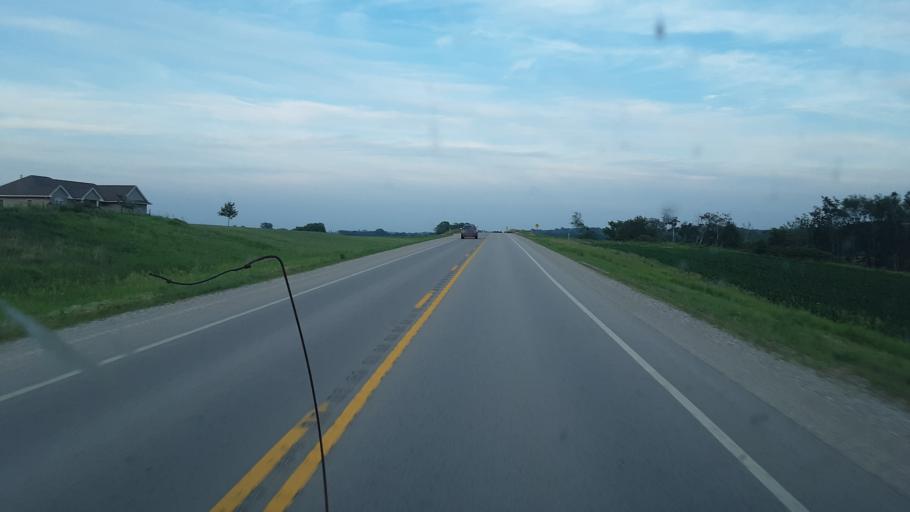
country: US
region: Iowa
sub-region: Benton County
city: Belle Plaine
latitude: 41.7425
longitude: -92.2491
